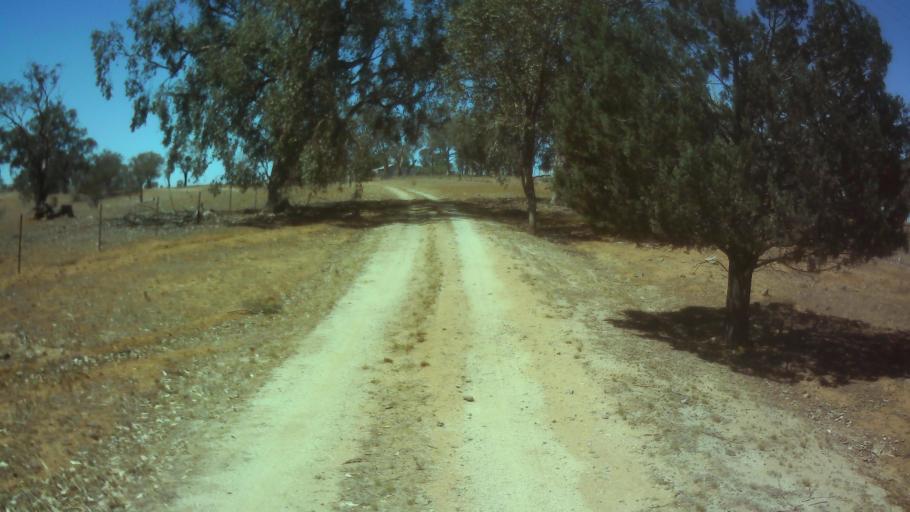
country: AU
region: New South Wales
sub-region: Cowra
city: Cowra
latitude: -33.8871
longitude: 148.4981
